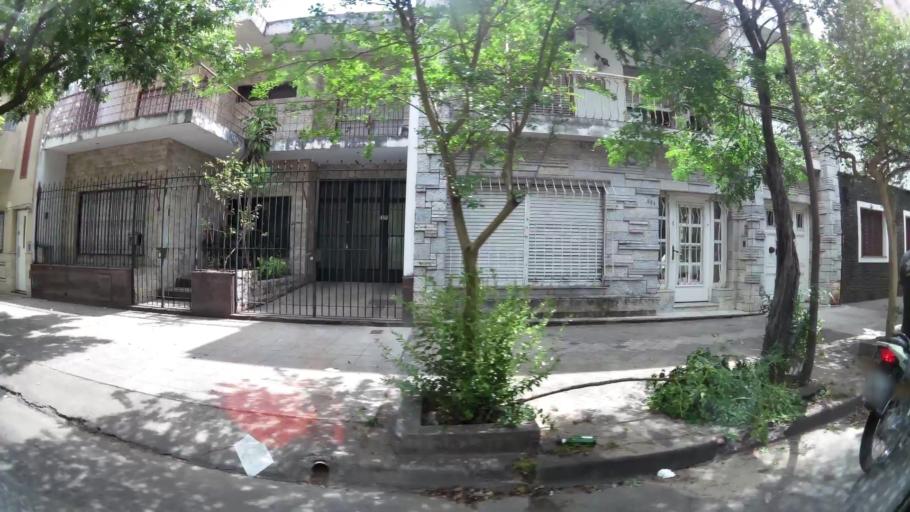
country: AR
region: Santa Fe
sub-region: Departamento de Rosario
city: Rosario
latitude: -32.9600
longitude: -60.6391
